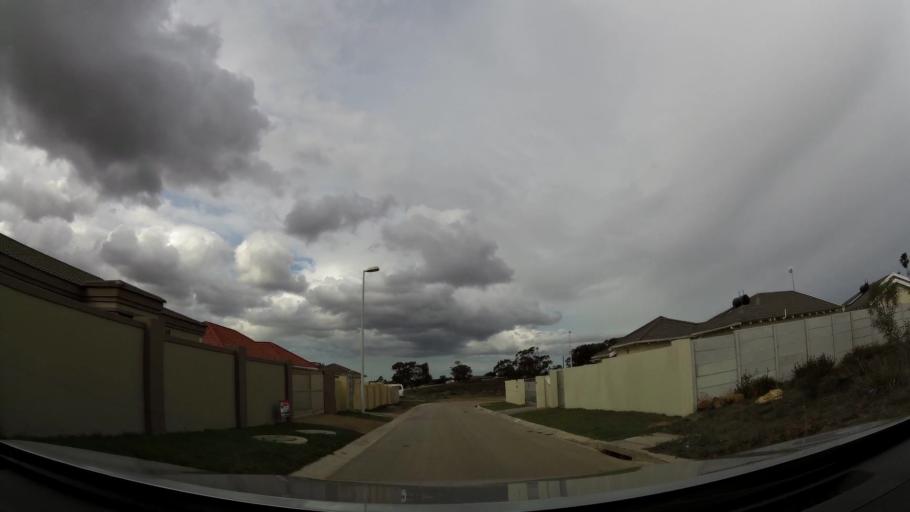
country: ZA
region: Eastern Cape
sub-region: Nelson Mandela Bay Metropolitan Municipality
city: Port Elizabeth
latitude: -33.9324
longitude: 25.5040
